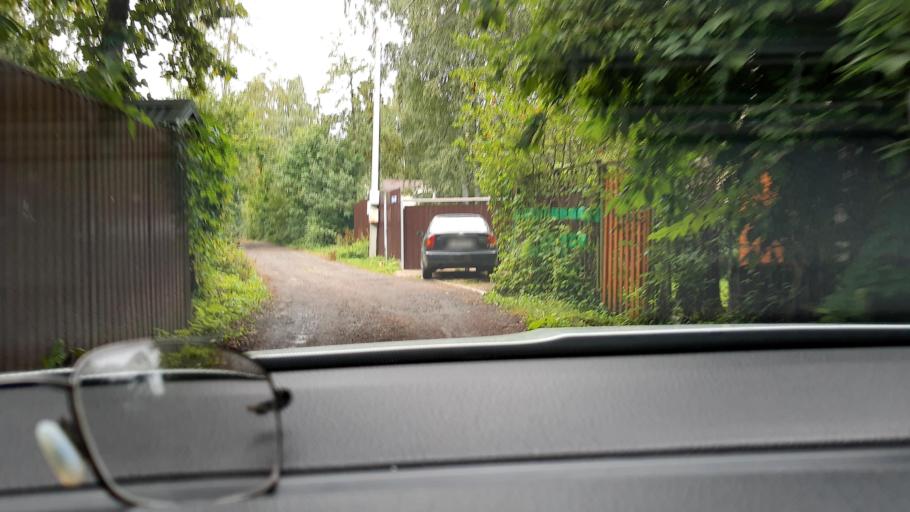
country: RU
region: Moskovskaya
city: Opalikha
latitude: 55.8285
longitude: 37.2895
